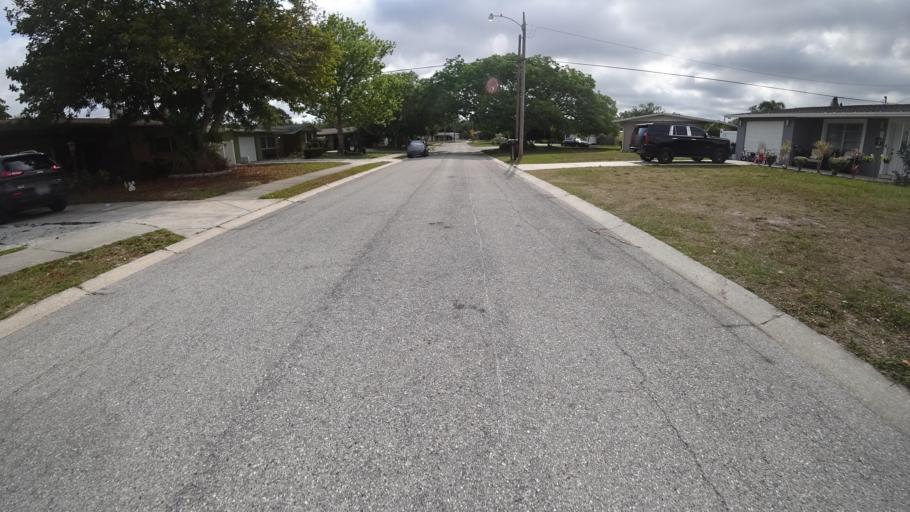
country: US
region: Florida
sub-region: Manatee County
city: South Bradenton
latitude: 27.4669
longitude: -82.6146
